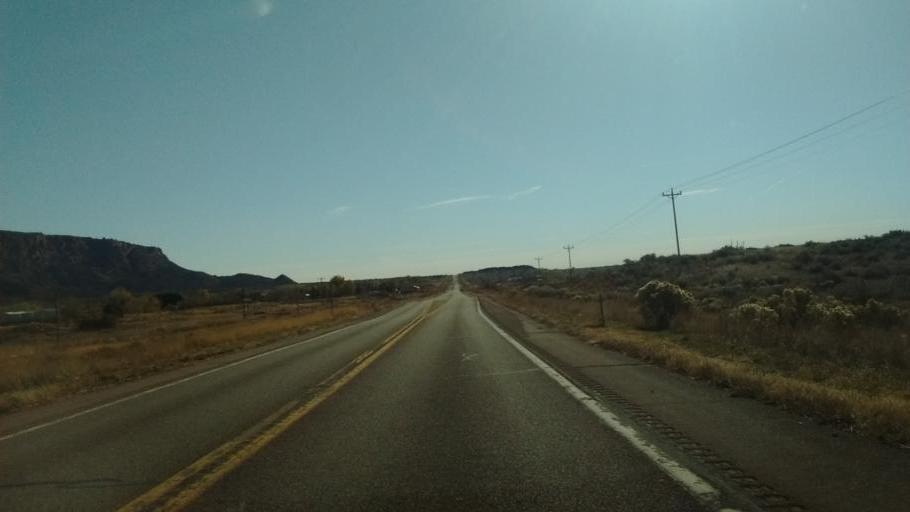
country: US
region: Arizona
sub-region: Mohave County
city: Colorado City
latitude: 36.9921
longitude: -112.9923
